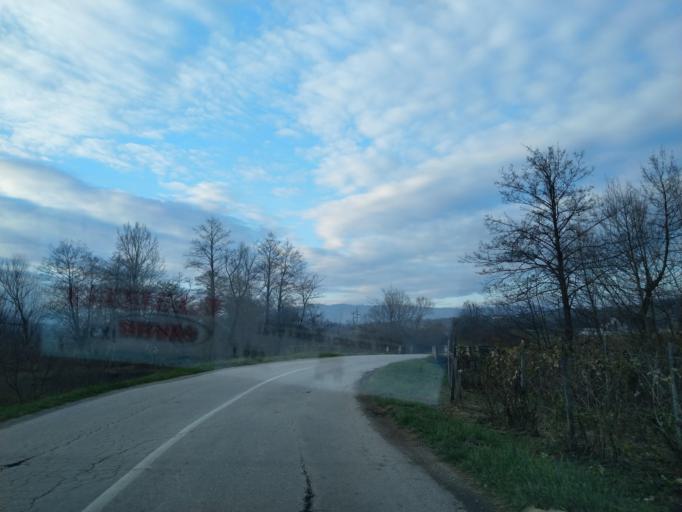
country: RS
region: Central Serbia
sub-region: Zlatiborski Okrug
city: Kosjeric
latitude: 43.9257
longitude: 19.8981
